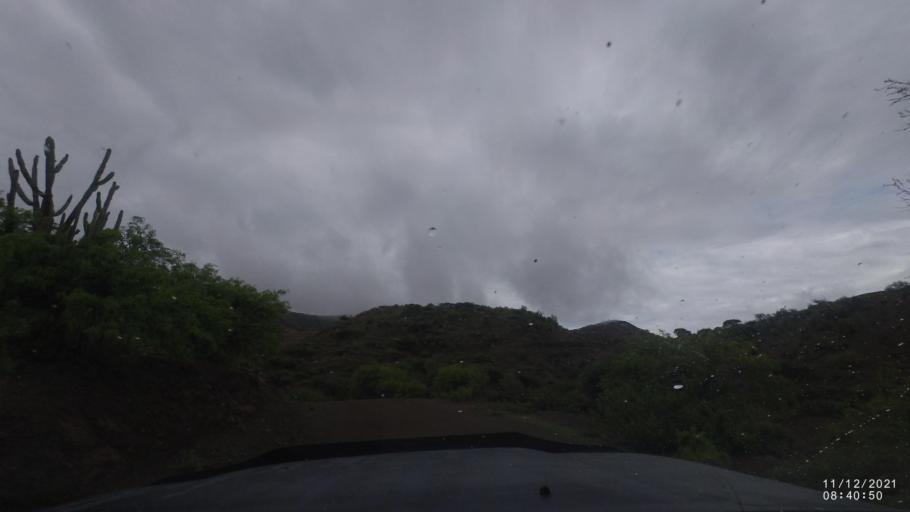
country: BO
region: Cochabamba
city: Tarata
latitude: -17.9178
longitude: -65.9341
